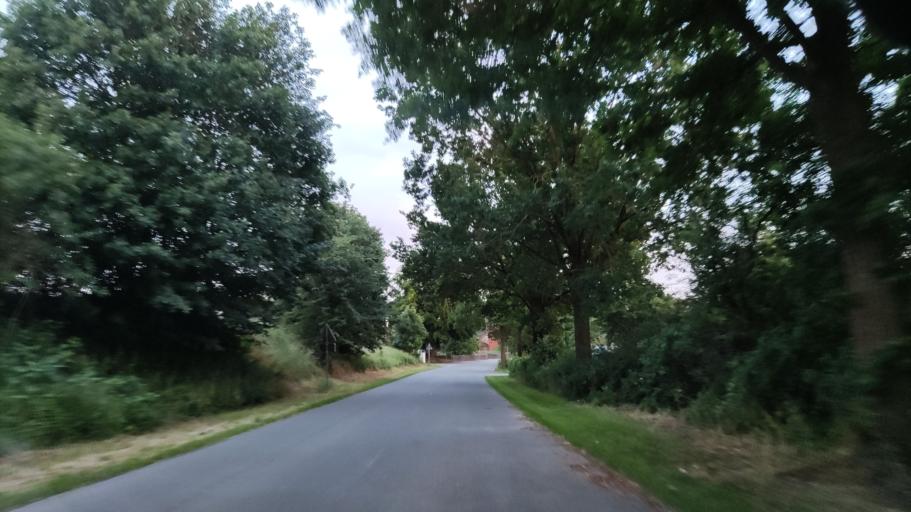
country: DE
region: Lower Saxony
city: Neu Darchau
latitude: 53.1889
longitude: 10.9306
